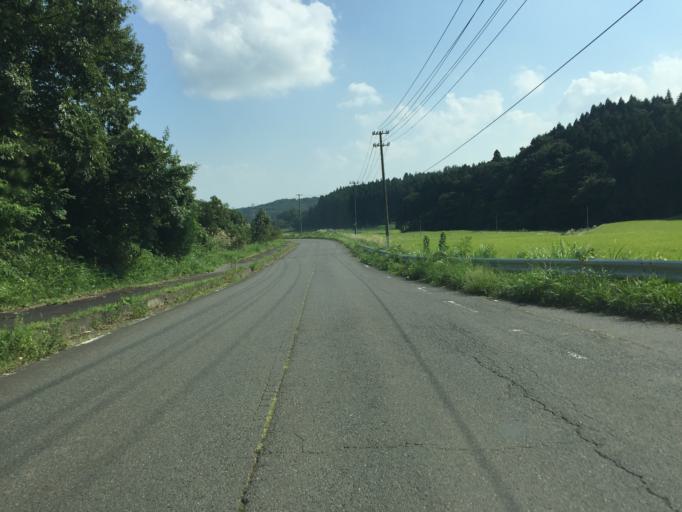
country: JP
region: Fukushima
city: Nihommatsu
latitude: 37.6077
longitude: 140.3958
